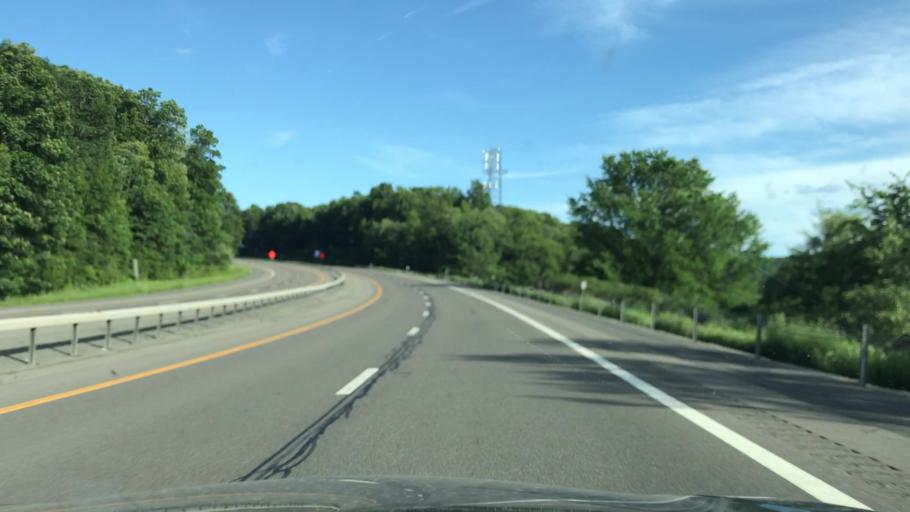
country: US
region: New York
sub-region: Delaware County
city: Hancock
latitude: 41.9566
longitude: -75.3149
